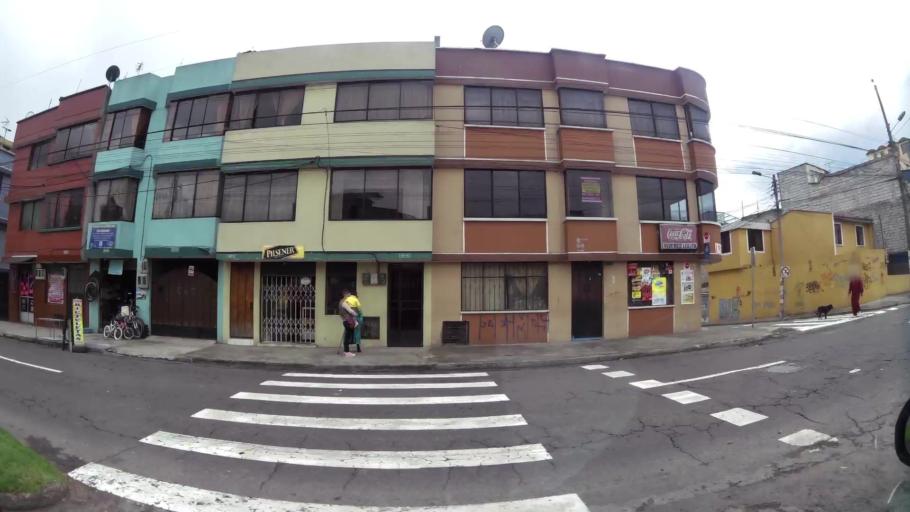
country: EC
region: Pichincha
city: Quito
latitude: -0.2756
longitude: -78.5452
